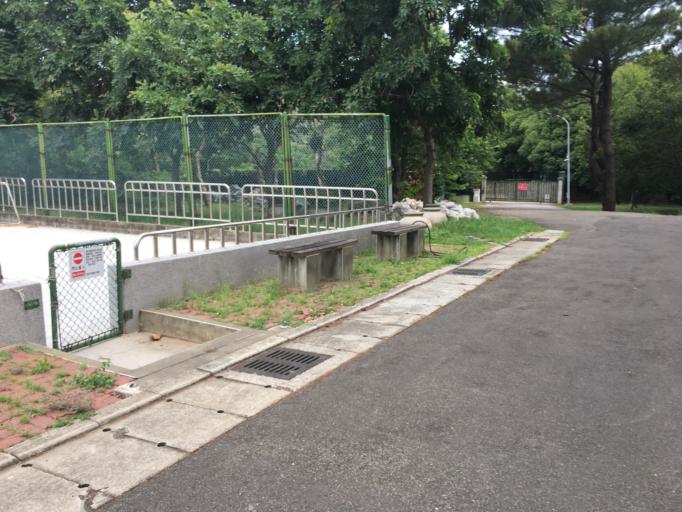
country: TW
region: Taiwan
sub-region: Hsinchu
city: Hsinchu
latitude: 24.7884
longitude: 120.9938
